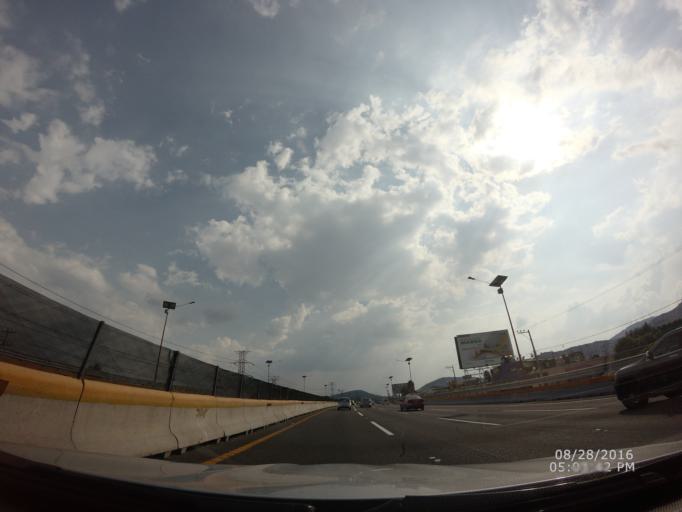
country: MX
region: Mexico
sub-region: Tlalnepantla de Baz
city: Puerto Escondido (Tepeolulco Puerto Escondido)
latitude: 19.5349
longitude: -99.0769
